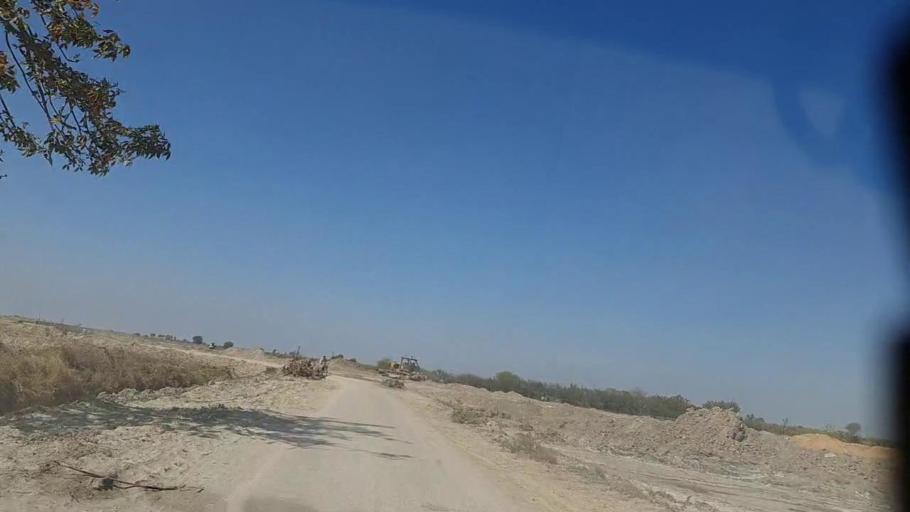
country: PK
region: Sindh
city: Mirwah Gorchani
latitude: 25.2262
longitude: 69.0193
